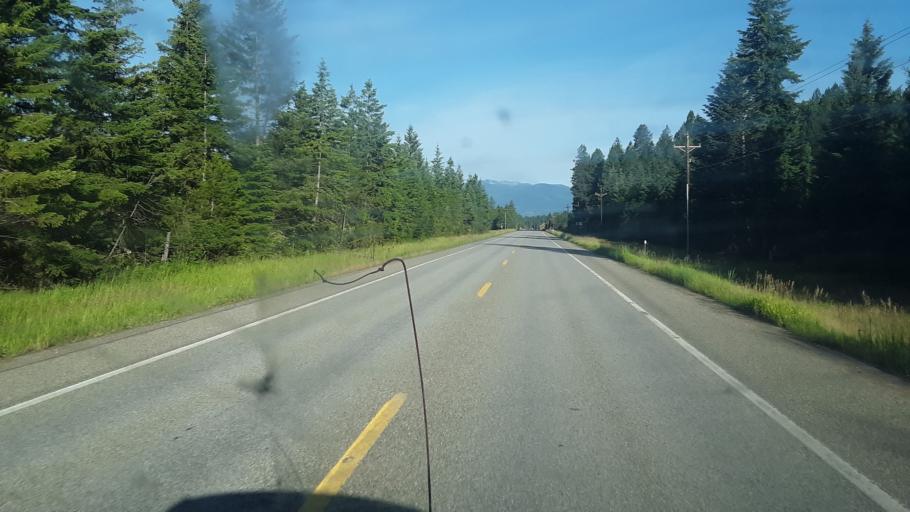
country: US
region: Idaho
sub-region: Boundary County
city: Bonners Ferry
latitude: 48.7276
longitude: -116.2182
